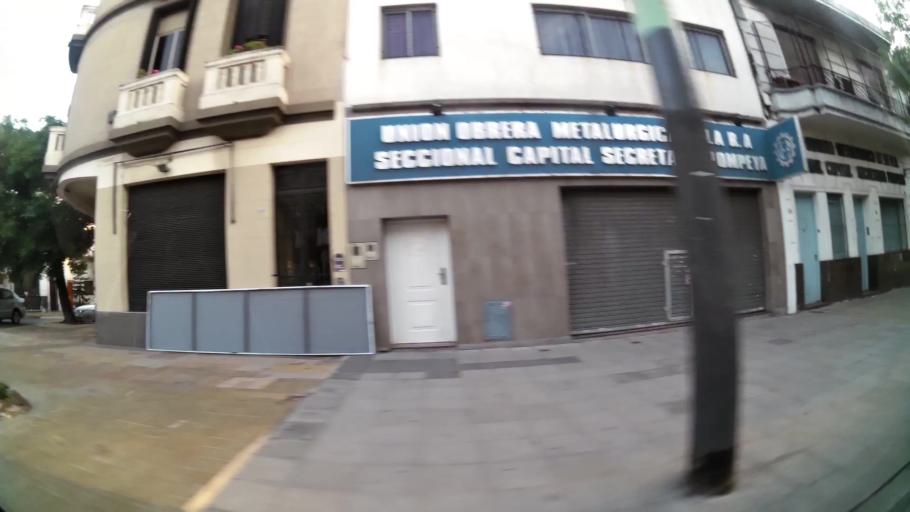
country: AR
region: Buenos Aires F.D.
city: Buenos Aires
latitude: -34.6401
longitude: -58.4225
